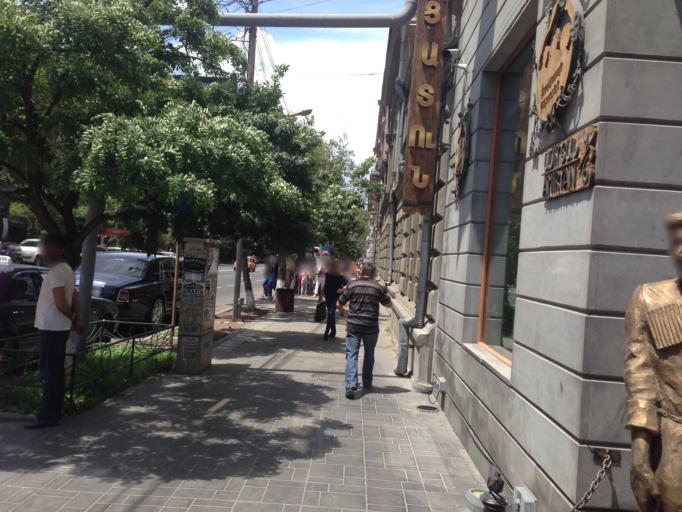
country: AM
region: Yerevan
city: Yerevan
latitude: 40.1791
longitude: 44.5103
